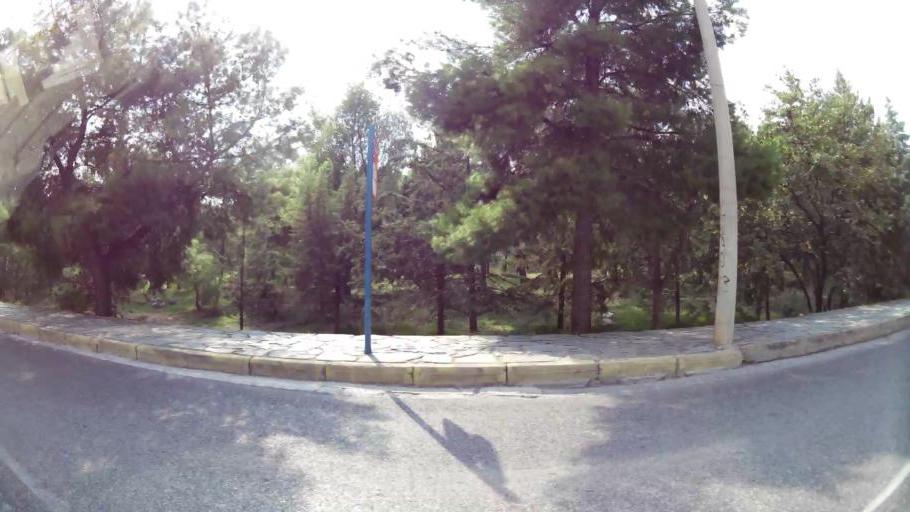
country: GR
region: Attica
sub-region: Nomarchia Athinas
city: Petroupolis
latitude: 38.0488
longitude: 23.6868
